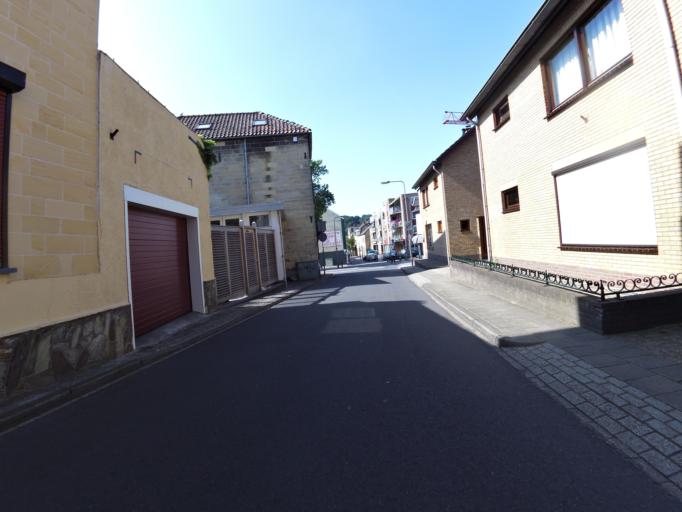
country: NL
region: Limburg
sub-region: Valkenburg aan de Geul
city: Valkenburg
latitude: 50.8664
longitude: 5.8353
